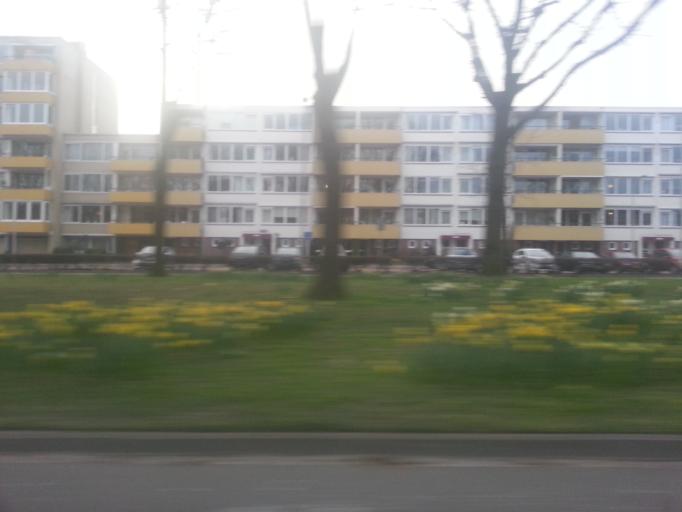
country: NL
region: North Brabant
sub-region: Gemeente Eindhoven
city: Eindhoven
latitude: 51.4487
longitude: 5.4772
